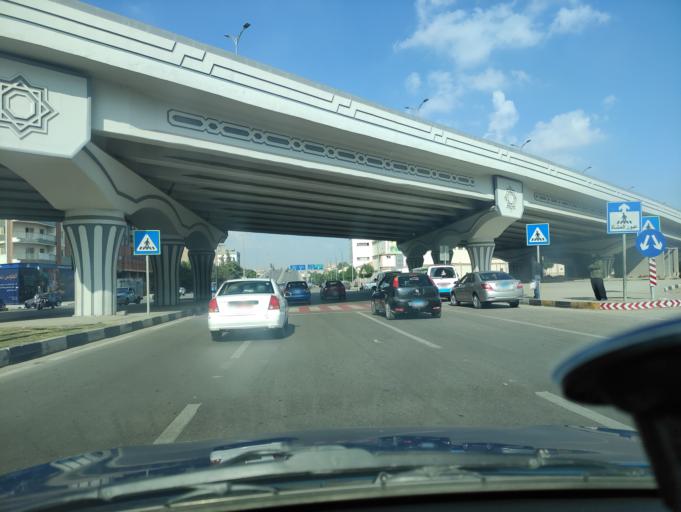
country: EG
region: Muhafazat al Qahirah
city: Cairo
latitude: 30.0905
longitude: 31.3416
